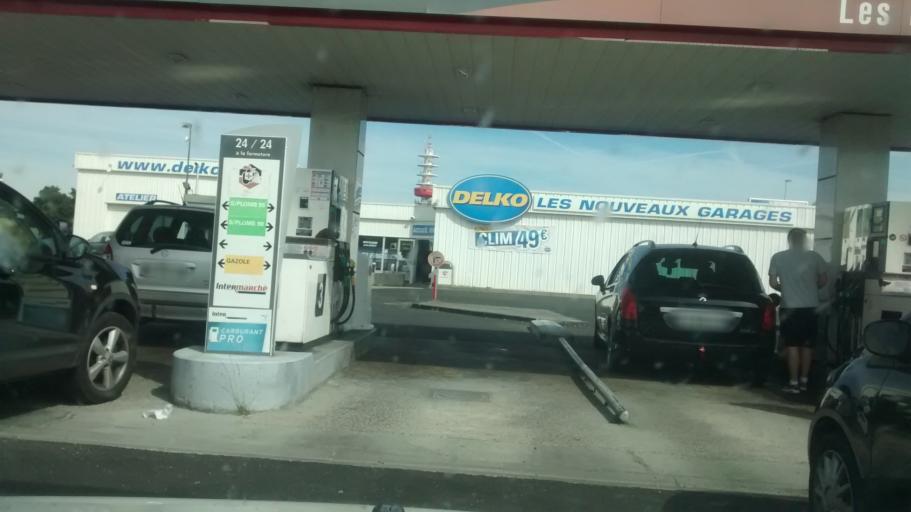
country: FR
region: Aquitaine
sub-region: Departement de la Gironde
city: Artigues-pres-Bordeaux
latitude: 44.8469
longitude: -0.4977
